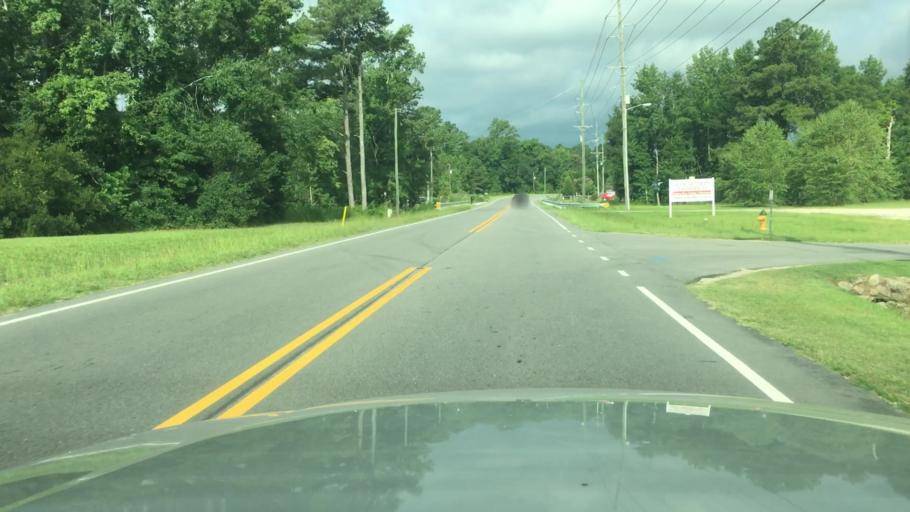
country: US
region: North Carolina
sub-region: Cumberland County
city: Hope Mills
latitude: 34.9470
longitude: -78.8710
